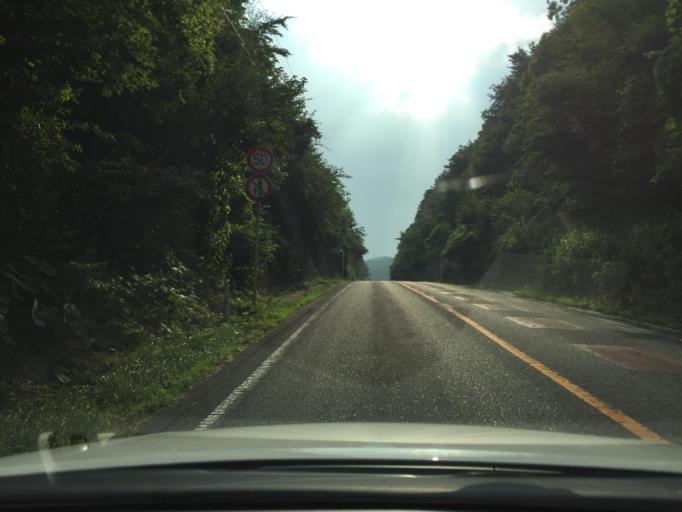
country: JP
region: Miyagi
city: Marumori
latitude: 37.6914
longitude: 140.8192
